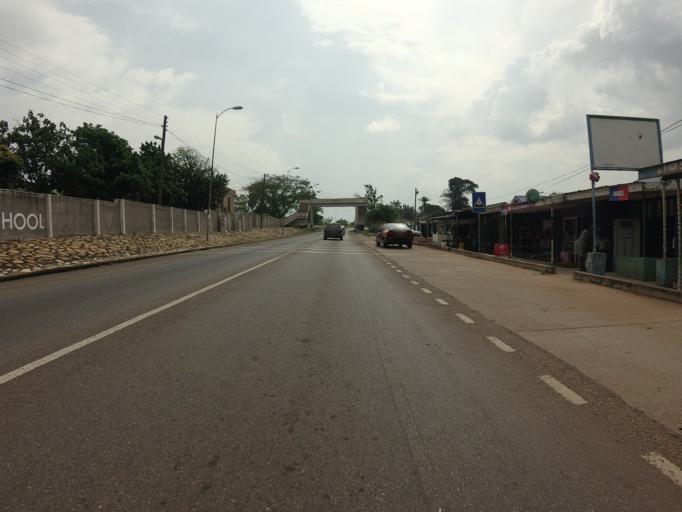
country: GH
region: Eastern
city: Aburi
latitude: 5.8391
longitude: -0.1764
